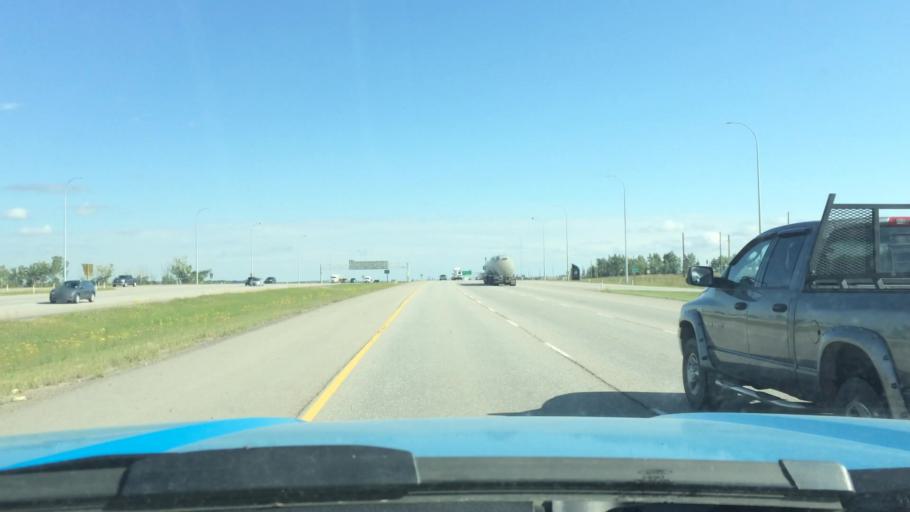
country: CA
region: Alberta
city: Airdrie
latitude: 51.1821
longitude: -114.0011
